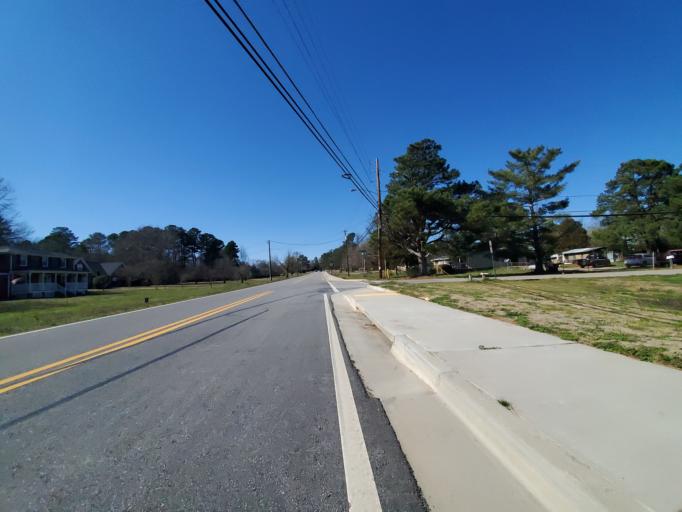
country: US
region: Georgia
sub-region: Gwinnett County
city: Dacula
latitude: 33.9795
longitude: -83.8780
